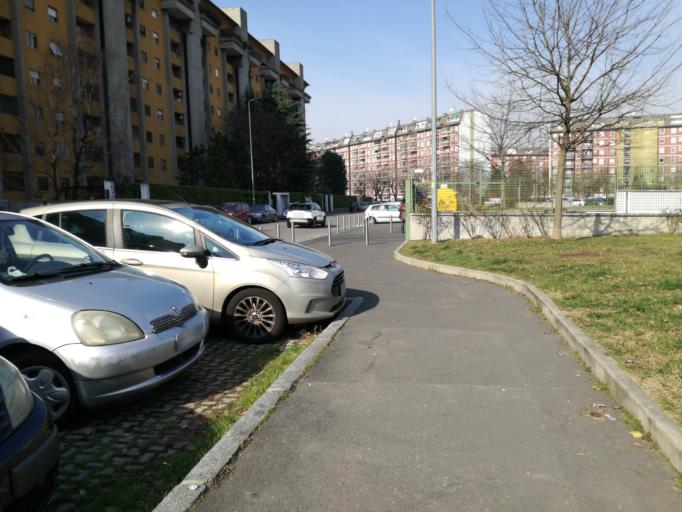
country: IT
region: Lombardy
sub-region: Citta metropolitana di Milano
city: Assago
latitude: 45.4274
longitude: 9.1530
